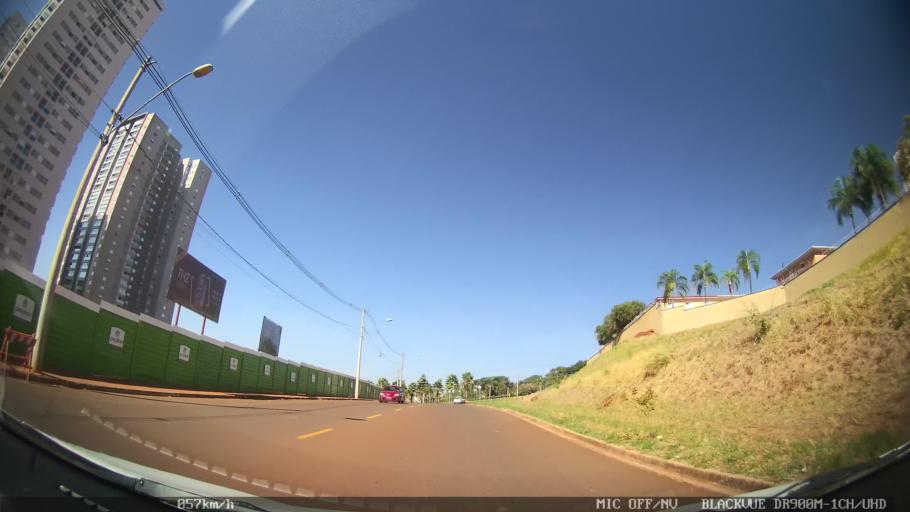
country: BR
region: Sao Paulo
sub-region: Ribeirao Preto
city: Ribeirao Preto
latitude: -21.2180
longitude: -47.8013
